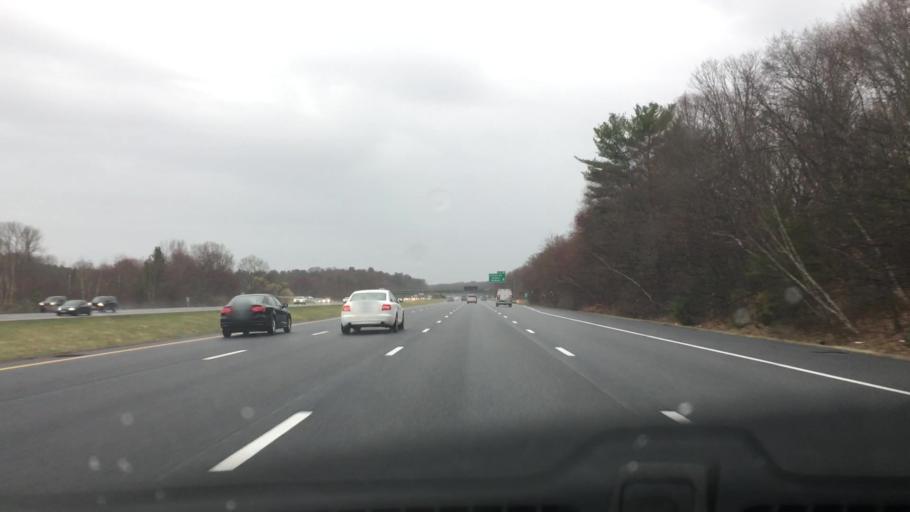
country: US
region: Massachusetts
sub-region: Essex County
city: West Newbury
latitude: 42.7613
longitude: -70.9390
